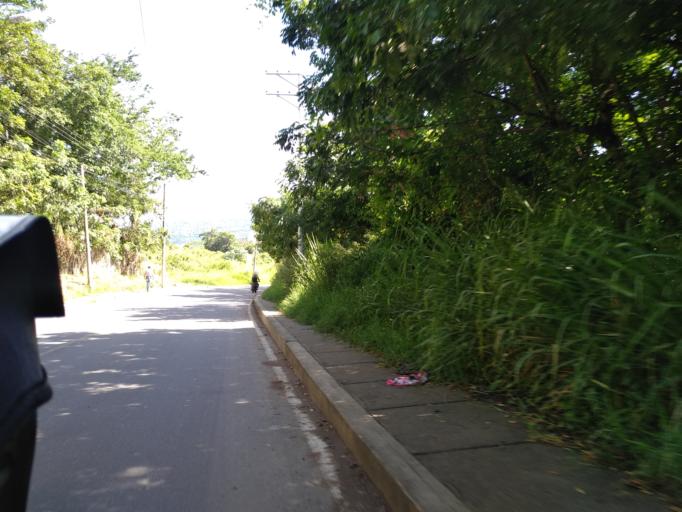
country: CO
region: Santander
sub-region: San Gil
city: San Gil
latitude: 6.5433
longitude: -73.1275
